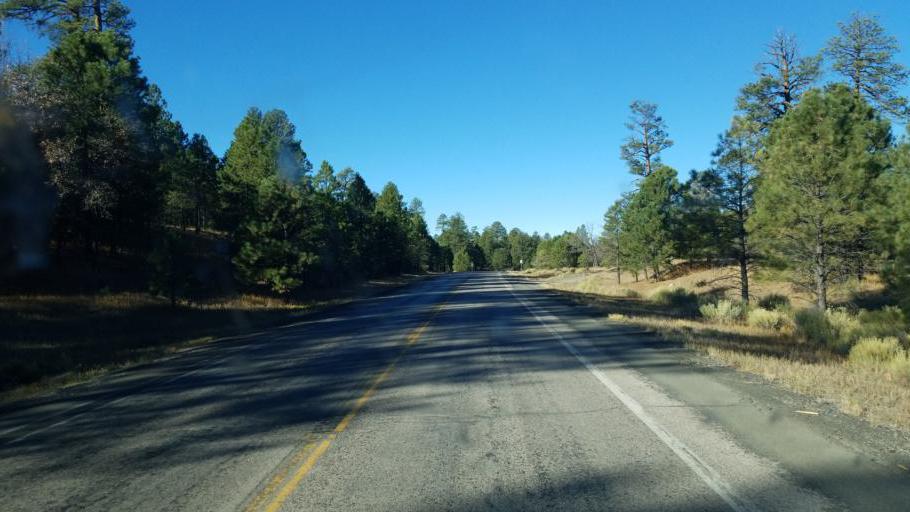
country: US
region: New Mexico
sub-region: McKinley County
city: Navajo
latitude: 36.0738
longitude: -108.9199
